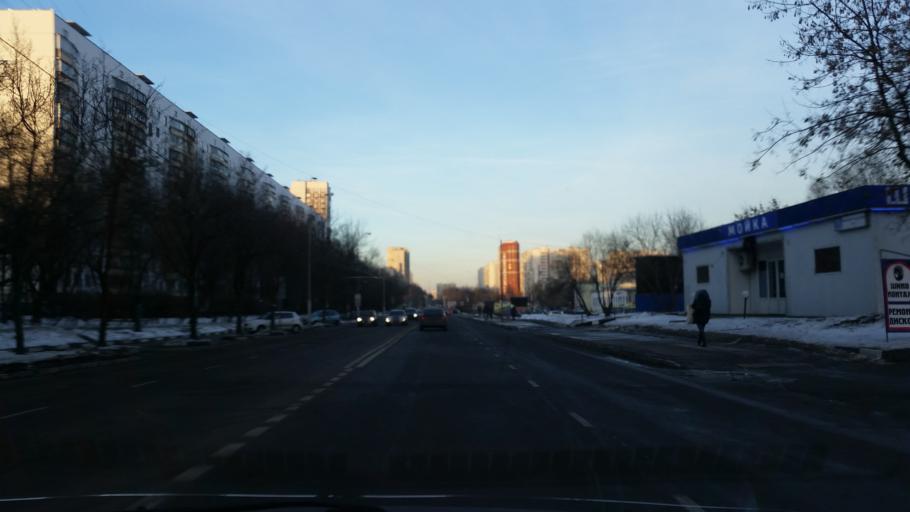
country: RU
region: Moscow
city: Chertanovo Yuzhnoye
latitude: 55.6176
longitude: 37.6065
